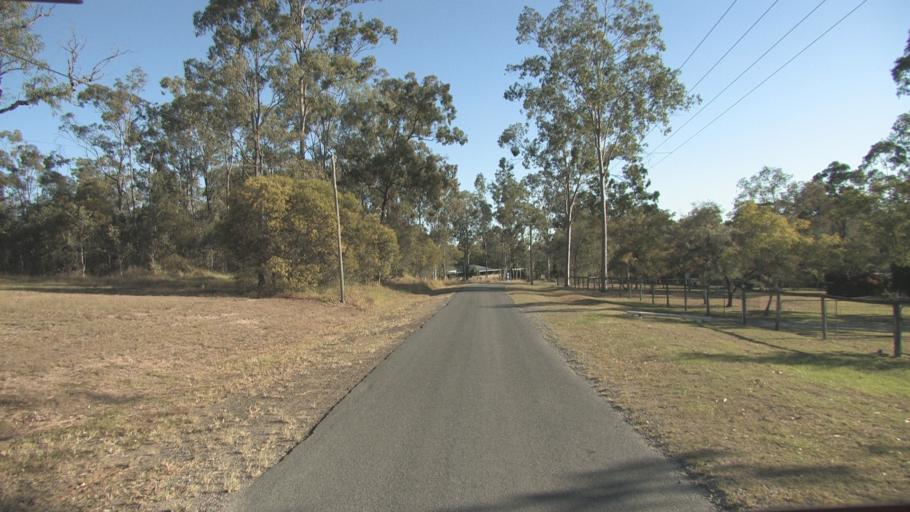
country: AU
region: Queensland
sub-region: Logan
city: North Maclean
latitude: -27.8126
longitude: 153.0464
